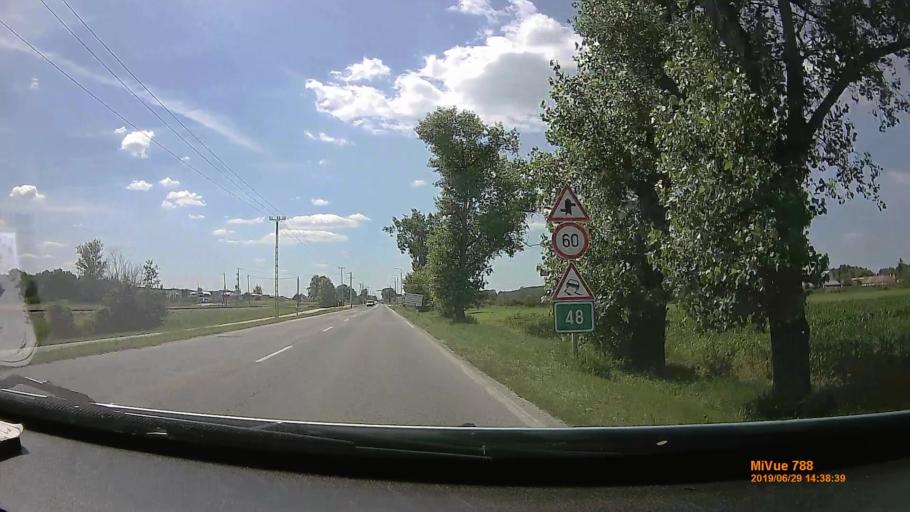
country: HU
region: Komarom-Esztergom
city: Tat
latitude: 47.7520
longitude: 18.6159
